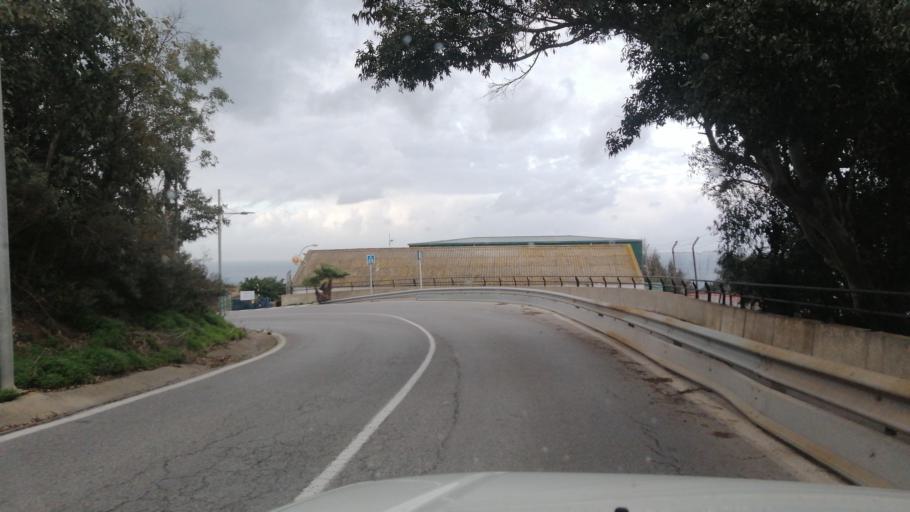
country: ES
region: Ceuta
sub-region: Ceuta
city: Ceuta
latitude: 35.9007
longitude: -5.2849
